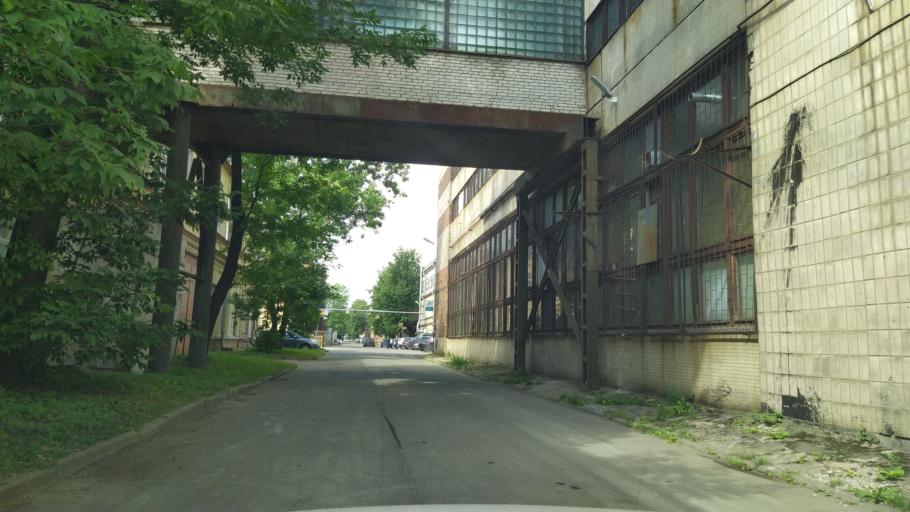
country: RU
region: Leningrad
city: Finlyandskiy
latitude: 59.9577
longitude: 30.3637
